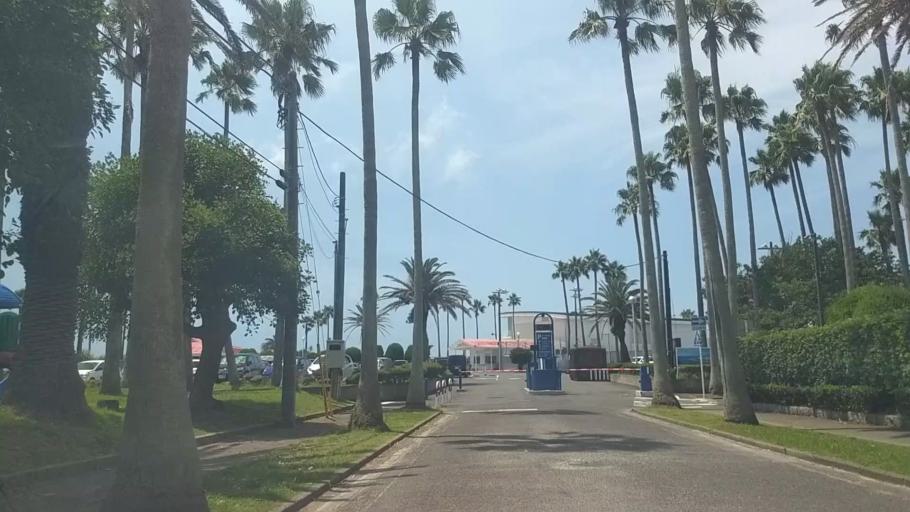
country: JP
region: Kanagawa
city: Kamakura
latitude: 35.2957
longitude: 139.5544
